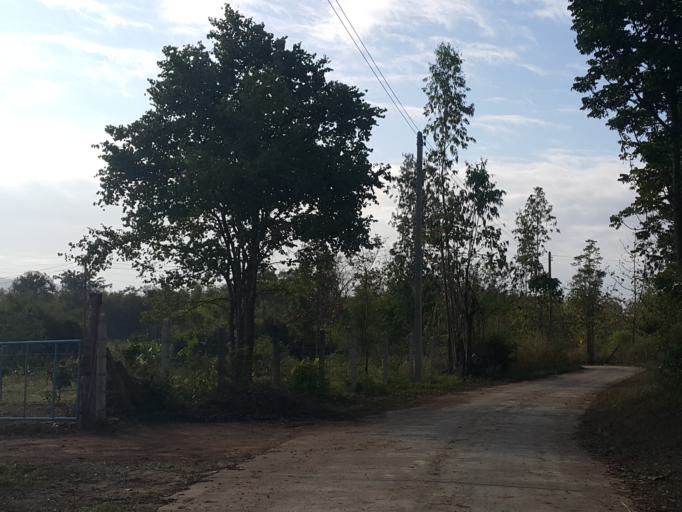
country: TH
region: Lampang
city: Mae Mo
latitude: 18.2548
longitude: 99.6016
